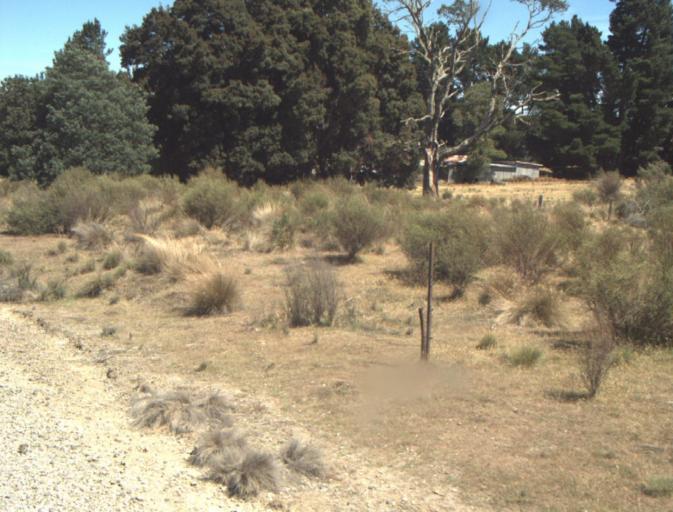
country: AU
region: Tasmania
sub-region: Dorset
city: Scottsdale
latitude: -41.3107
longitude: 147.4657
